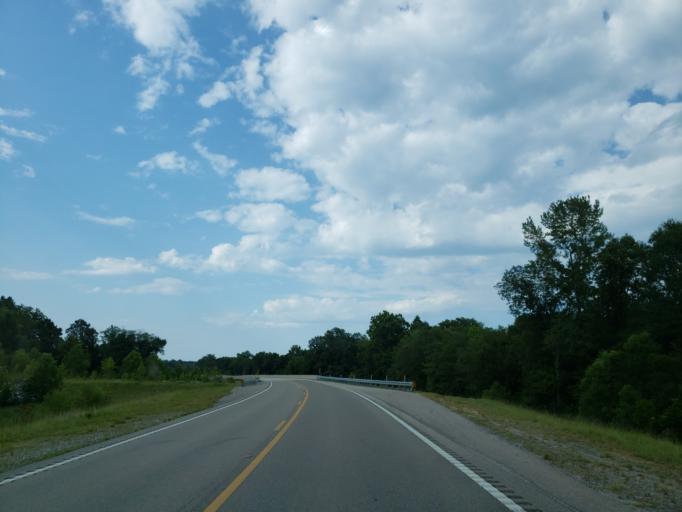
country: US
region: Mississippi
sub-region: Clarke County
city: Stonewall
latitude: 32.1692
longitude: -88.9314
